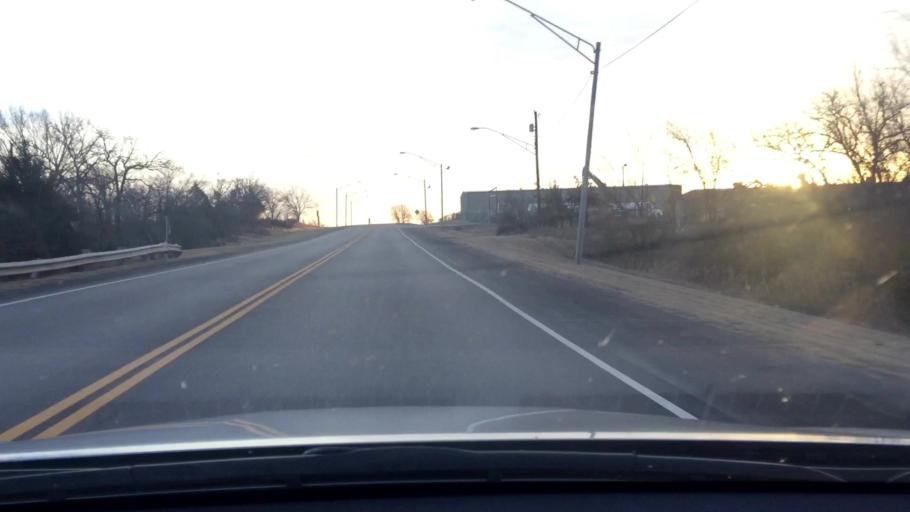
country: US
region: Oklahoma
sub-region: Carter County
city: Ardmore
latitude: 34.1749
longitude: -97.1744
